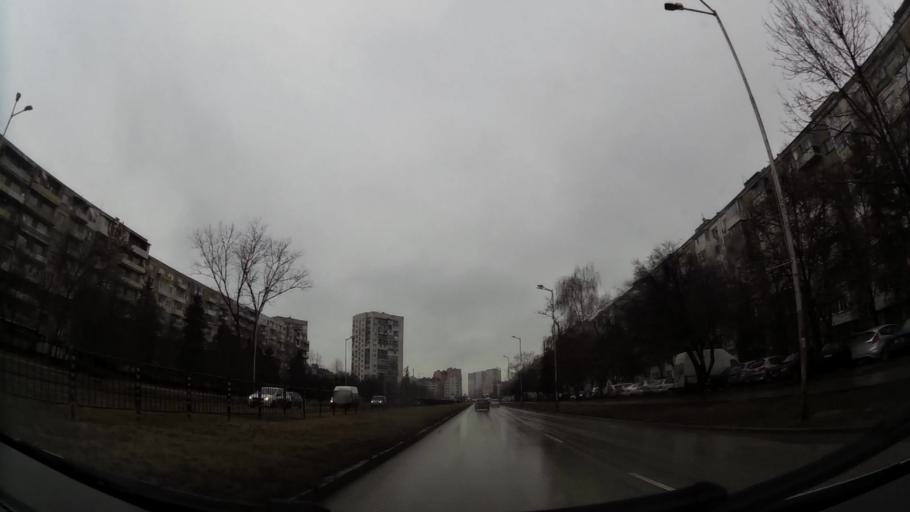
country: BG
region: Sofia-Capital
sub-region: Stolichna Obshtina
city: Sofia
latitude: 42.6518
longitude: 23.3747
